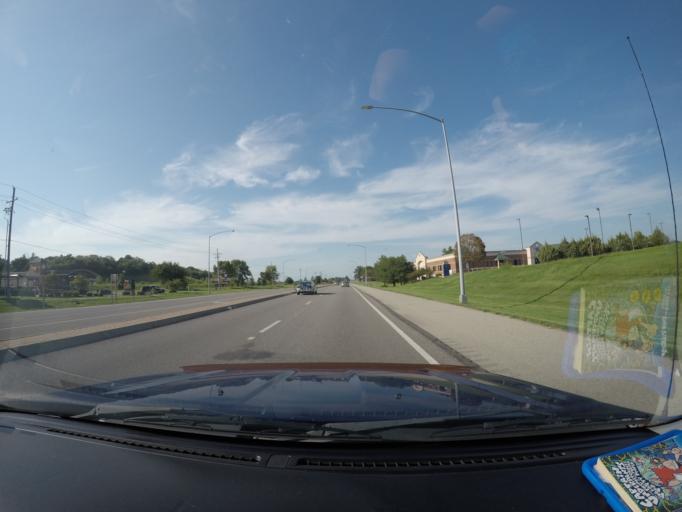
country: US
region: Kansas
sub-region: Leavenworth County
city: Lansing
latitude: 39.2385
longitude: -94.9001
